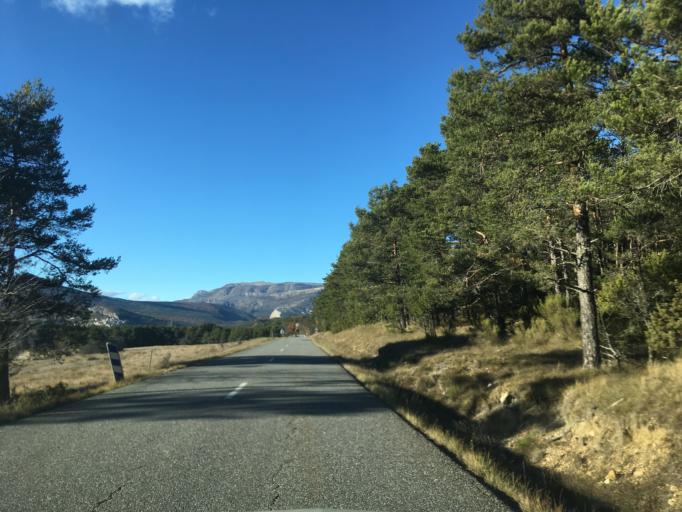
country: FR
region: Provence-Alpes-Cote d'Azur
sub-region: Departement des Alpes-de-Haute-Provence
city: Castellane
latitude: 43.7444
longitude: 6.4780
